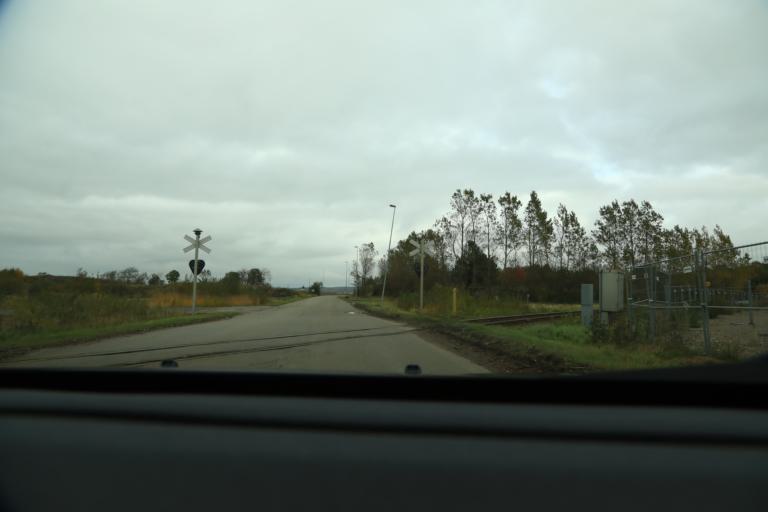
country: SE
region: Halland
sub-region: Varbergs Kommun
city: Varberg
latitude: 57.1201
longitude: 12.2433
